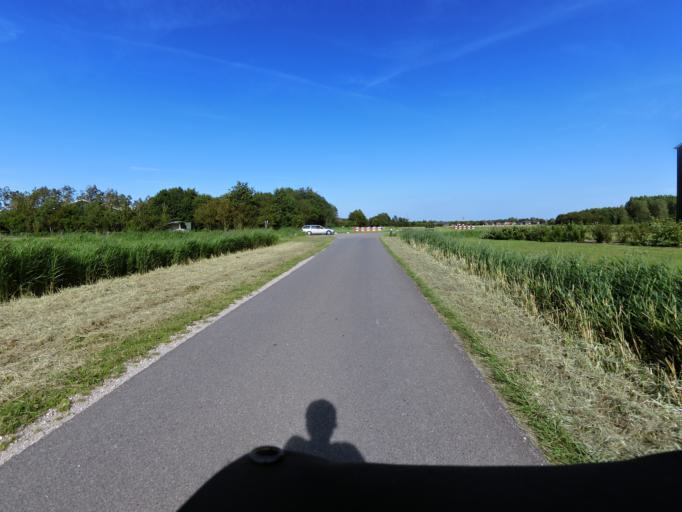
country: NL
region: South Holland
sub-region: Gemeente Goeree-Overflakkee
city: Dirksland
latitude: 51.7491
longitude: 4.0821
